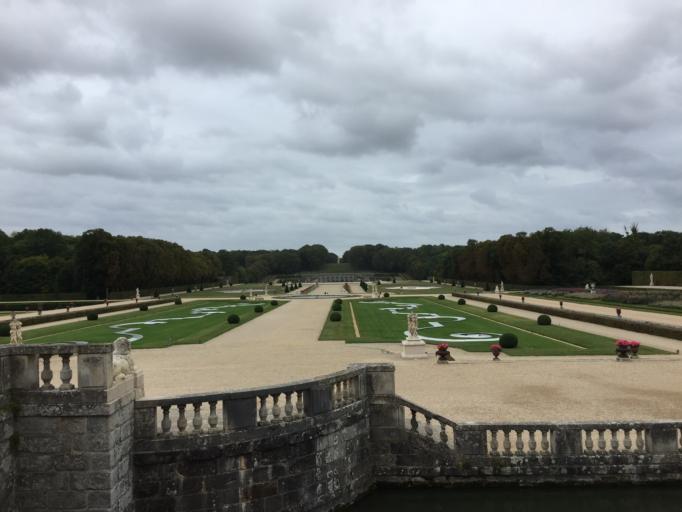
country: FR
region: Ile-de-France
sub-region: Departement de Seine-et-Marne
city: Maincy
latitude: 48.5656
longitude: 2.7140
